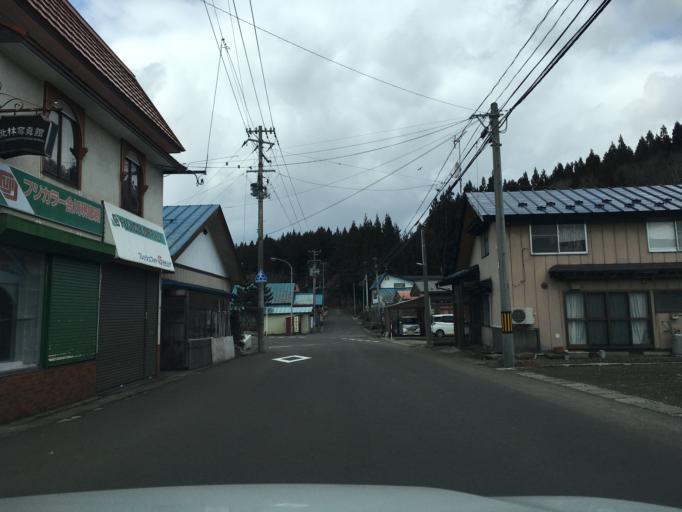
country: JP
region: Akita
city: Takanosu
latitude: 40.1619
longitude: 140.3286
